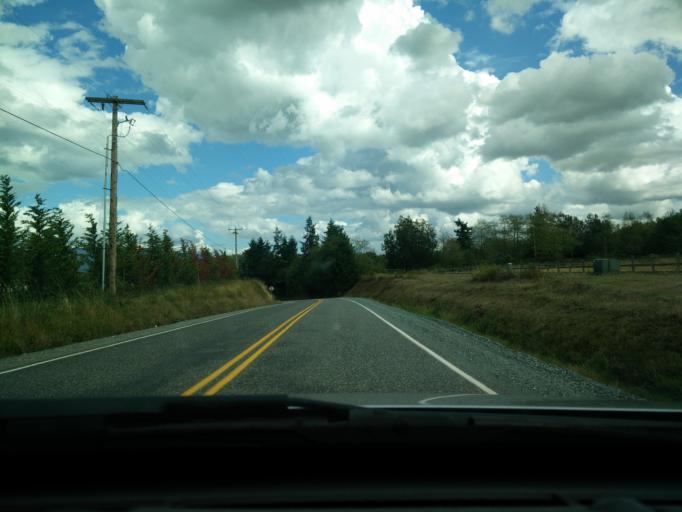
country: US
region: Washington
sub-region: Skagit County
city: Anacortes
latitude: 48.5157
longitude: -122.4764
